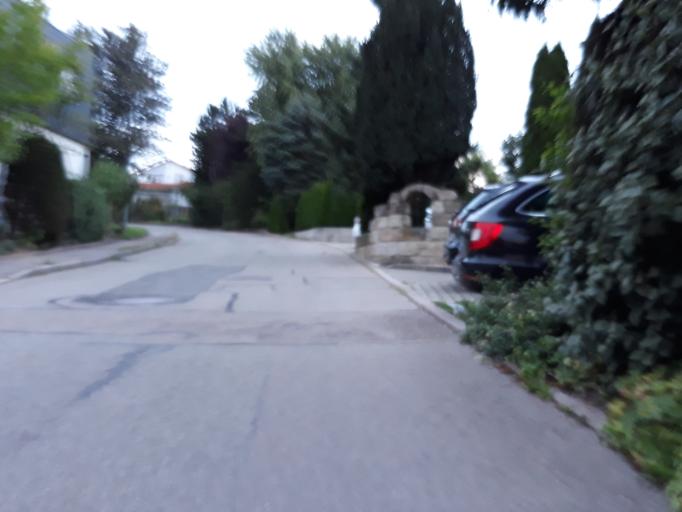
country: DE
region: Baden-Wuerttemberg
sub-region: Regierungsbezirk Stuttgart
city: Schonaich
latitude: 48.6659
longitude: 9.0639
